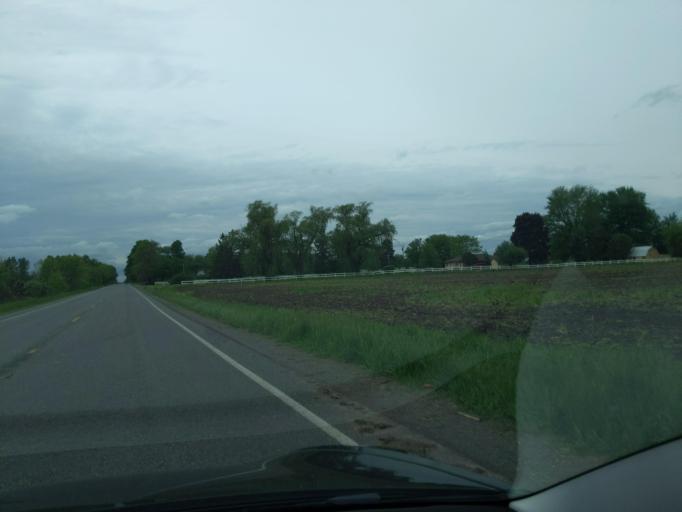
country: US
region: Michigan
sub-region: Ingham County
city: Mason
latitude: 42.6009
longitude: -84.4463
